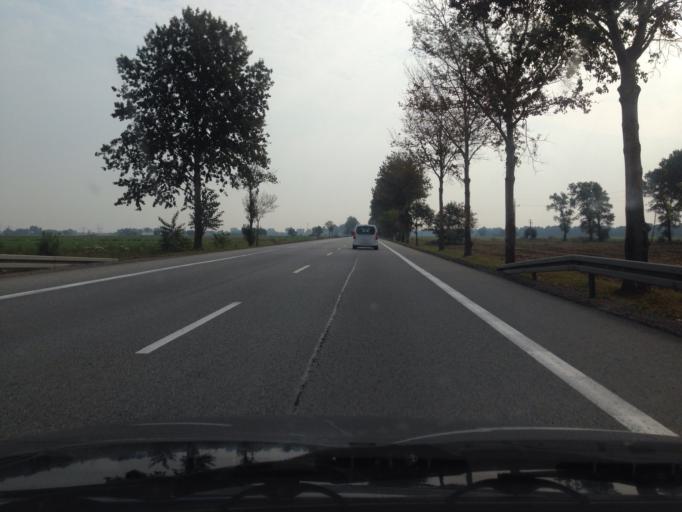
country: PL
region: Pomeranian Voivodeship
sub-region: Powiat gdanski
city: Cedry Wielkie
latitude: 54.2667
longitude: 18.8962
